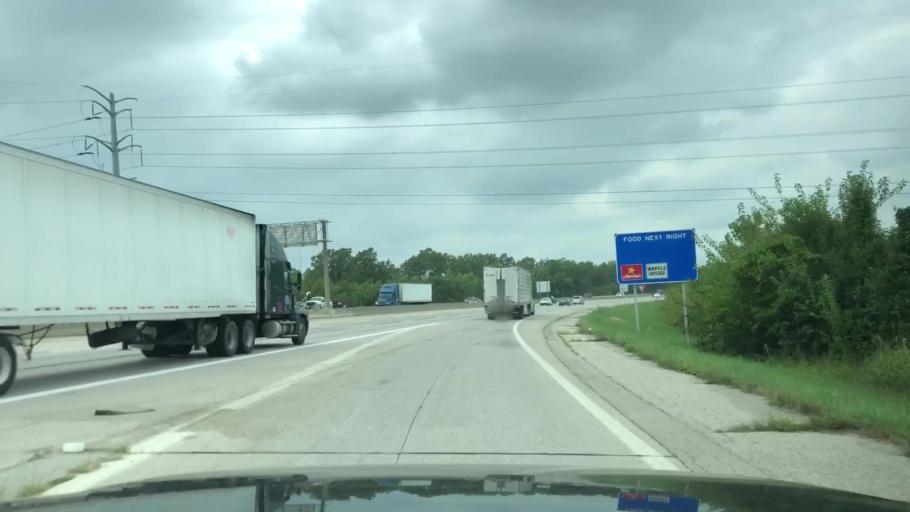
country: US
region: Missouri
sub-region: Saint Charles County
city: Saint Charles
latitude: 38.7927
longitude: -90.4558
